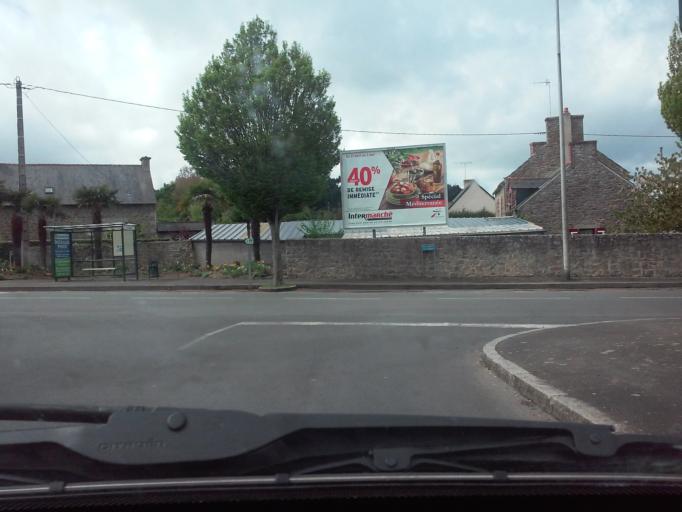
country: FR
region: Brittany
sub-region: Departement d'Ille-et-Vilaine
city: Dinard
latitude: 48.6298
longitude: -2.0754
